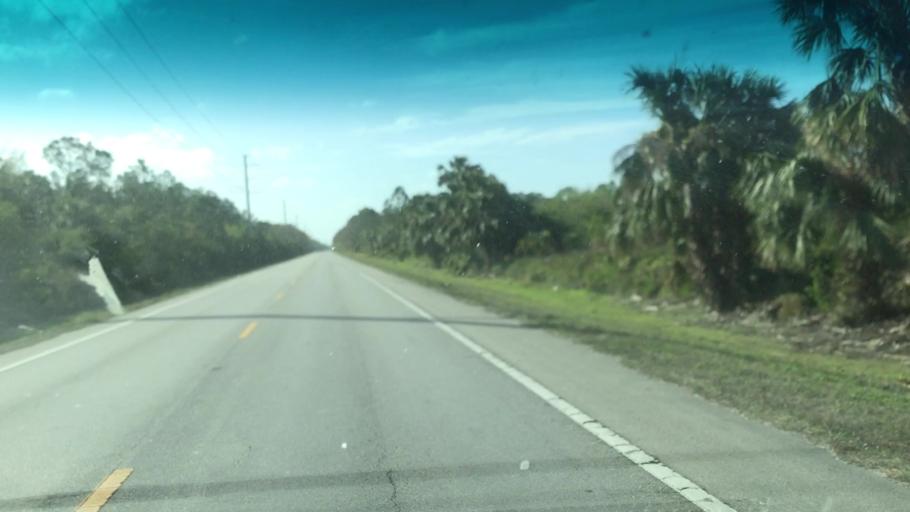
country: US
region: Florida
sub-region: Collier County
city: Orangetree
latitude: 26.3491
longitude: -81.5953
